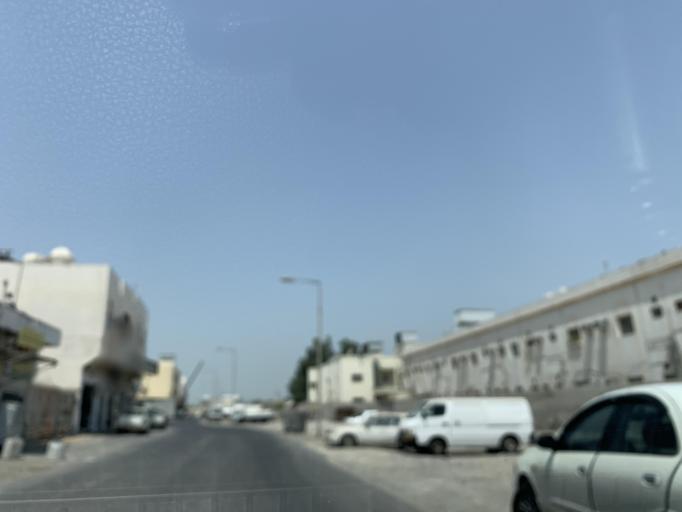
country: BH
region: Northern
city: Madinat `Isa
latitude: 26.1908
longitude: 50.5552
